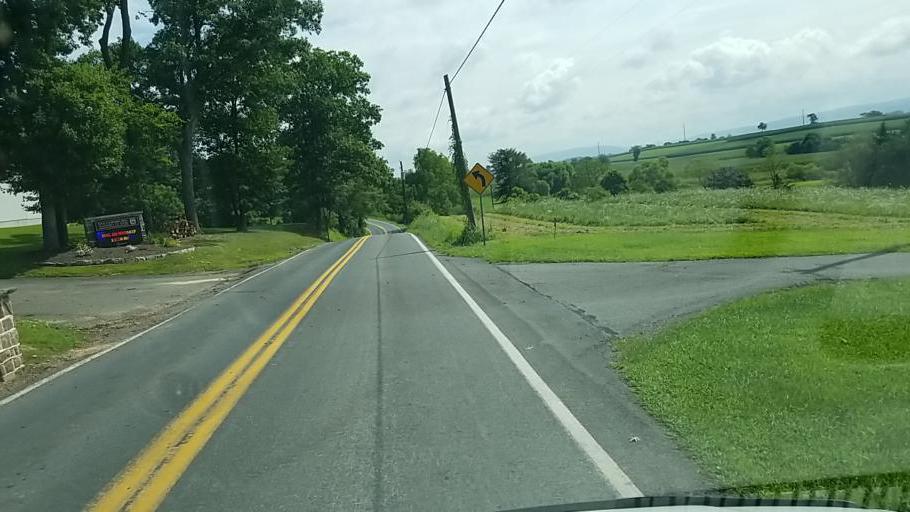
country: US
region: Pennsylvania
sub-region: Dauphin County
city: Millersburg
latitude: 40.5856
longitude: -76.9178
